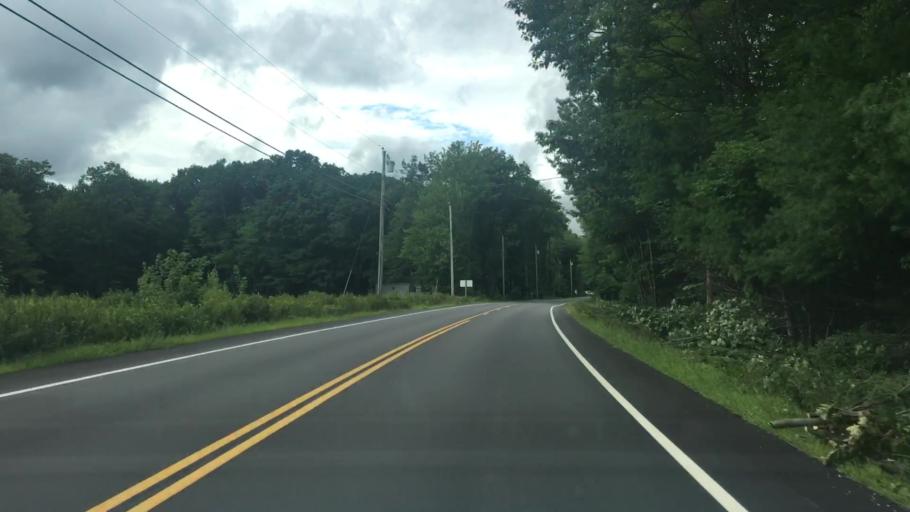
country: US
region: Maine
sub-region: York County
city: West Kennebunk
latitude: 43.4753
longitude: -70.6033
